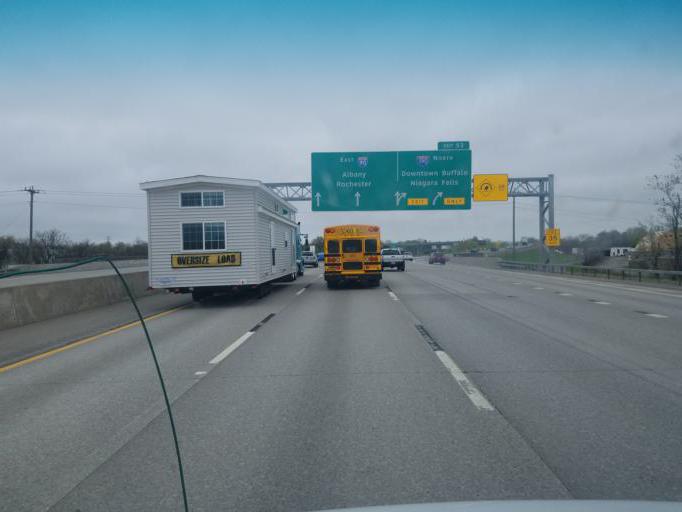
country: US
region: New York
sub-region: Erie County
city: West Seneca
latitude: 42.8706
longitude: -78.7896
